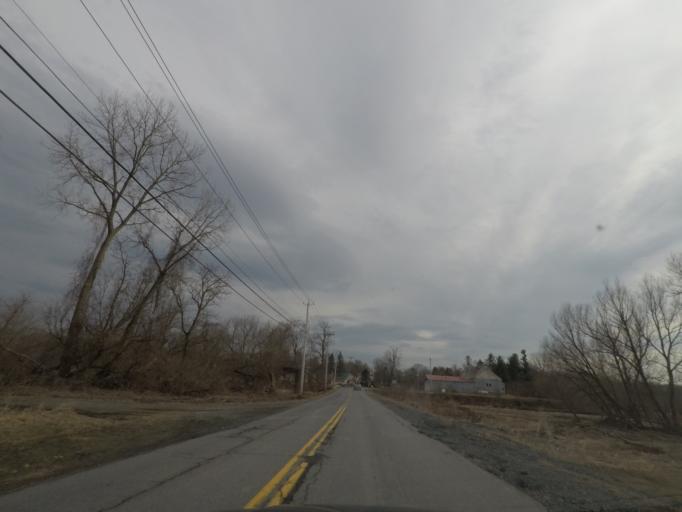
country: US
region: New York
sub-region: Washington County
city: Cambridge
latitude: 42.9572
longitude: -73.4330
